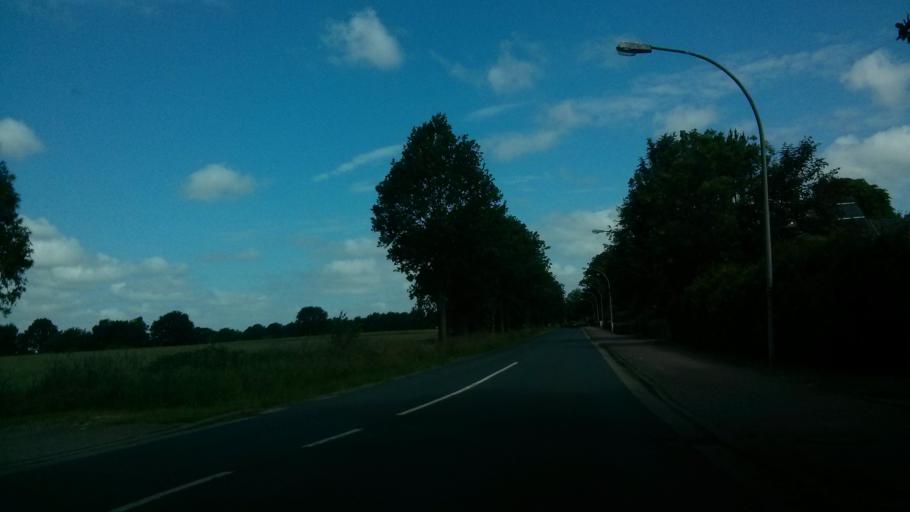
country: DE
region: Lower Saxony
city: Loxstedt
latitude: 53.4803
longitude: 8.6466
